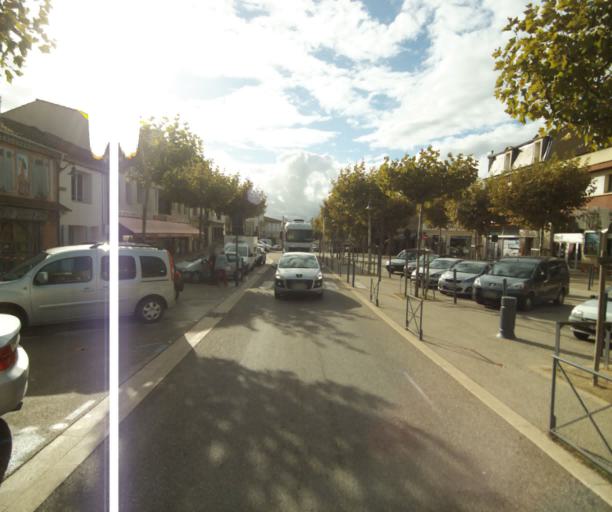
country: FR
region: Midi-Pyrenees
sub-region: Departement du Gers
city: Eauze
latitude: 43.8595
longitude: 0.1011
